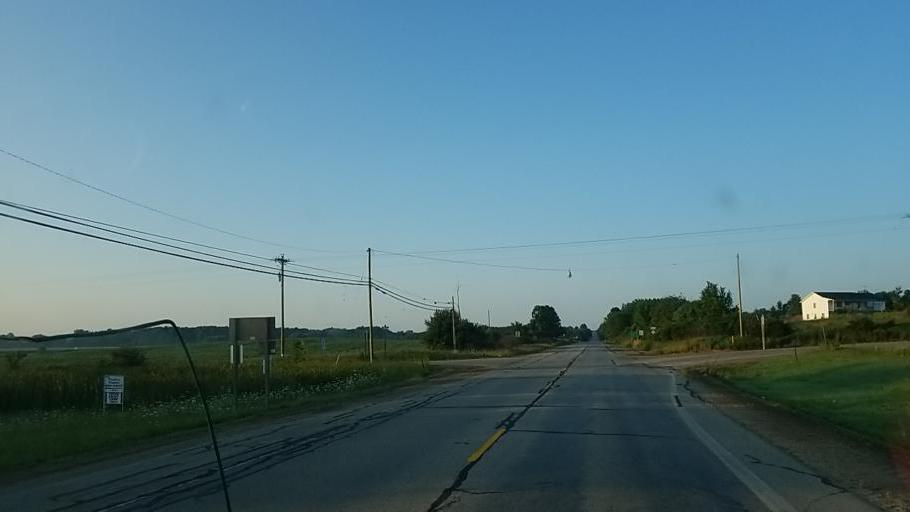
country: US
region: Michigan
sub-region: Isabella County
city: Lake Isabella
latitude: 43.7421
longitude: -85.1473
